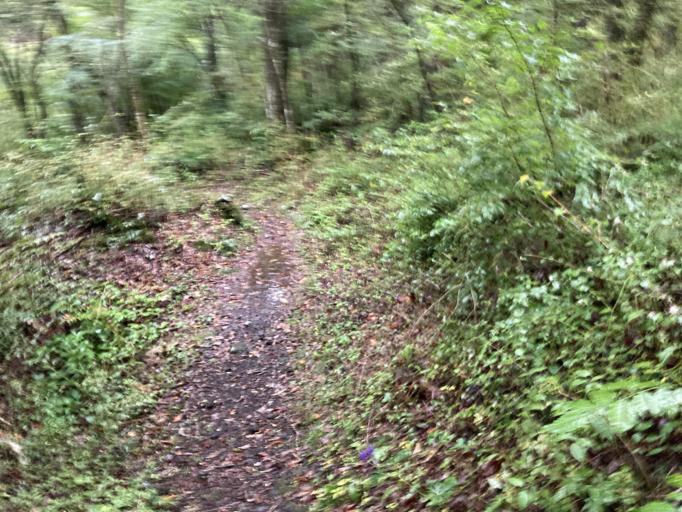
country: JP
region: Shizuoka
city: Fuji
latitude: 35.2439
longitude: 138.7283
